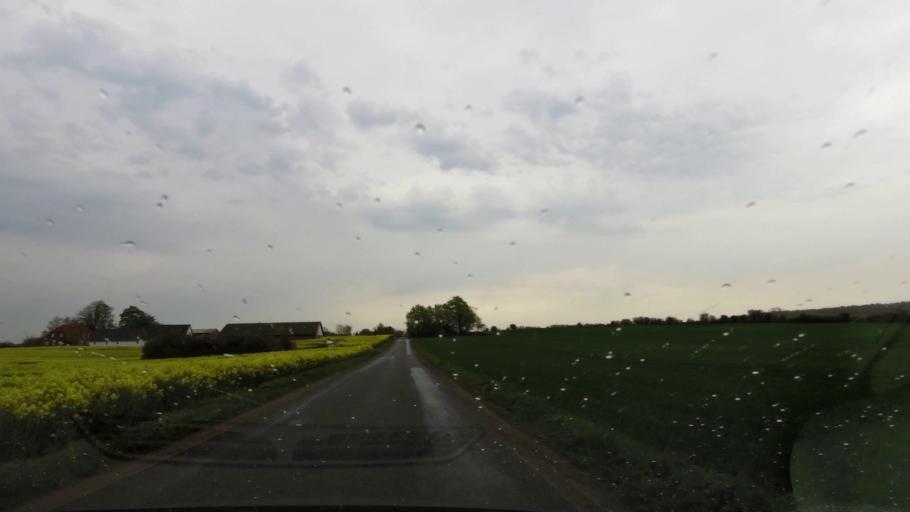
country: DK
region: South Denmark
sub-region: Faaborg-Midtfyn Kommune
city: Ringe
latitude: 55.1907
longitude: 10.5604
